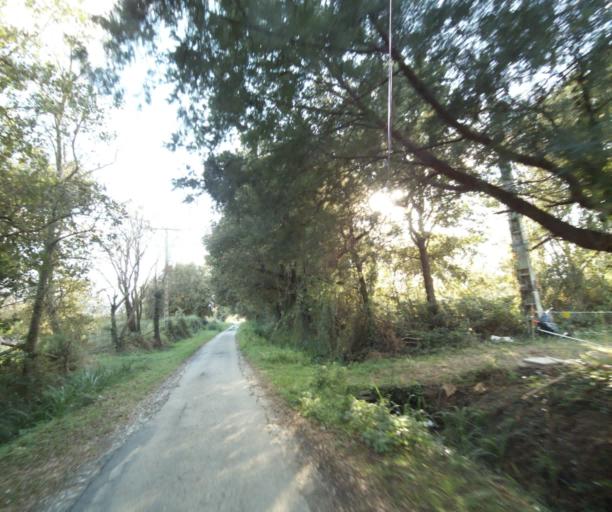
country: FR
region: Languedoc-Roussillon
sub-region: Departement des Pyrenees-Orientales
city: Argelers
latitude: 42.5636
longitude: 3.0197
